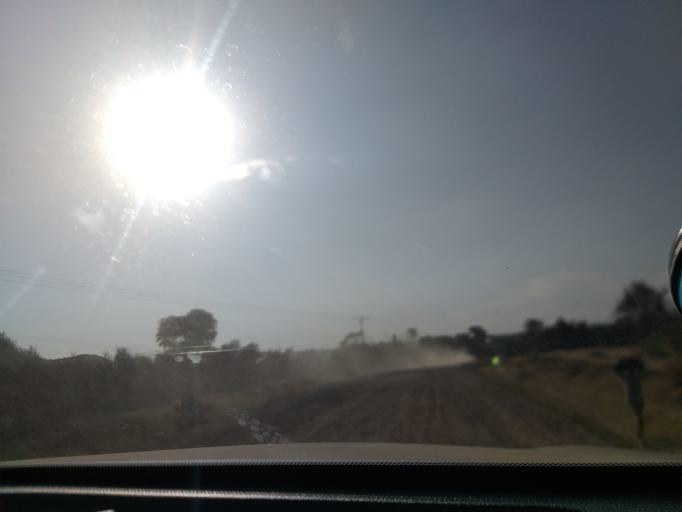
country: ET
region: Oromiya
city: Shashemene
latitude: 7.4893
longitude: 38.7426
